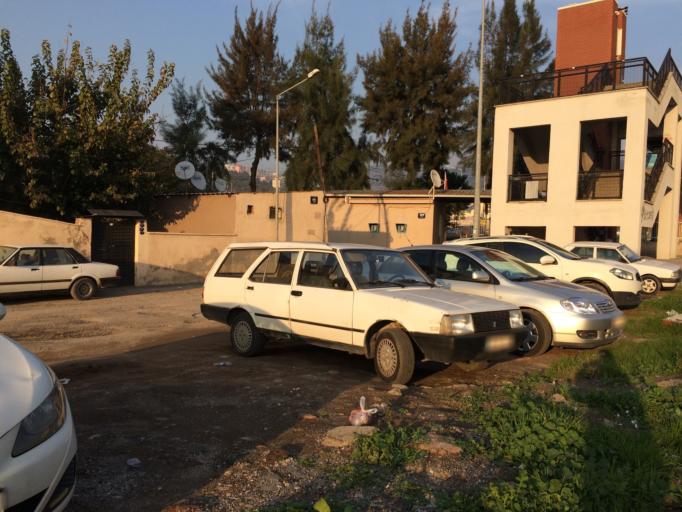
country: TR
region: Izmir
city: Karsiyaka
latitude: 38.4936
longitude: 27.0595
